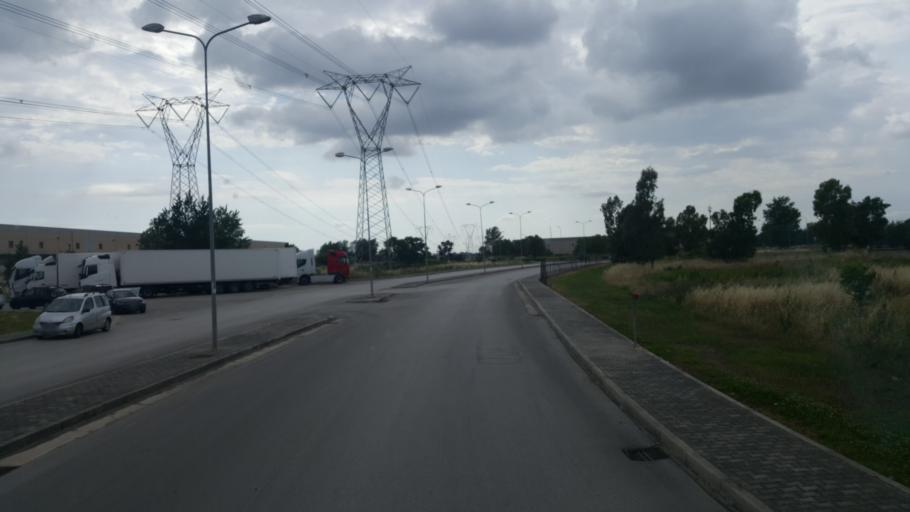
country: IT
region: Campania
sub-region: Provincia di Caserta
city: San Marco Evangelista
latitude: 41.0072
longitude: 14.3579
